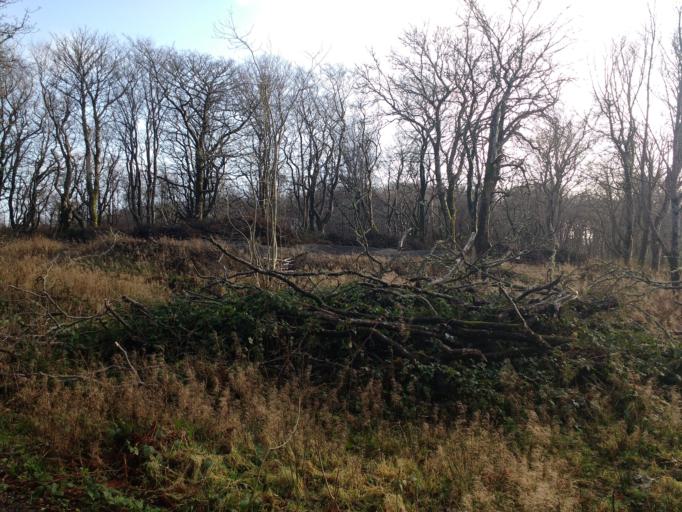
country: GB
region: Scotland
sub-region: Eilean Siar
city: Isle of Lewis
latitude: 58.2146
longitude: -6.3960
